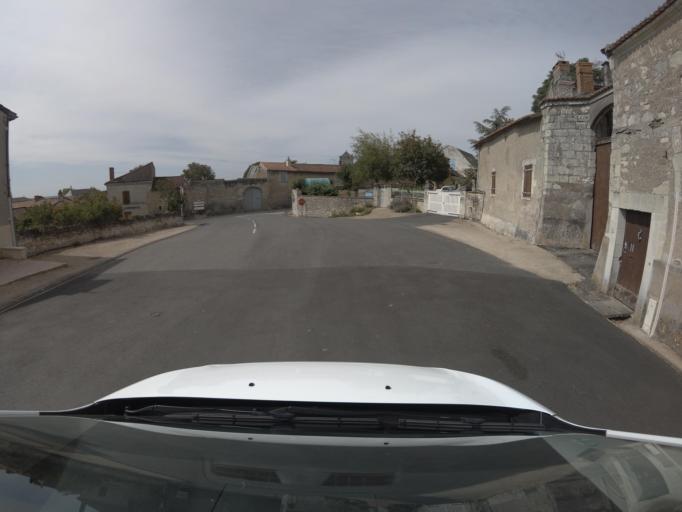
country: FR
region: Poitou-Charentes
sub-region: Departement des Deux-Sevres
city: Saint-Leger-de-Montbrun
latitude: 47.0129
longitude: -0.0572
